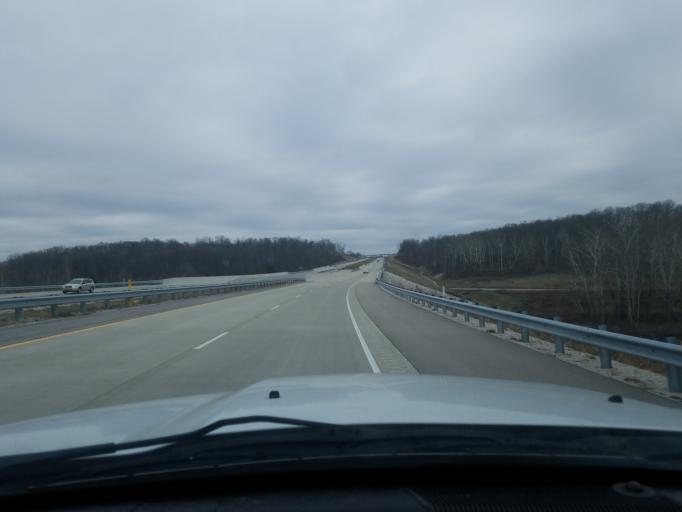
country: US
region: Indiana
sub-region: Monroe County
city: Ellettsville
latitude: 39.0676
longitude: -86.6763
